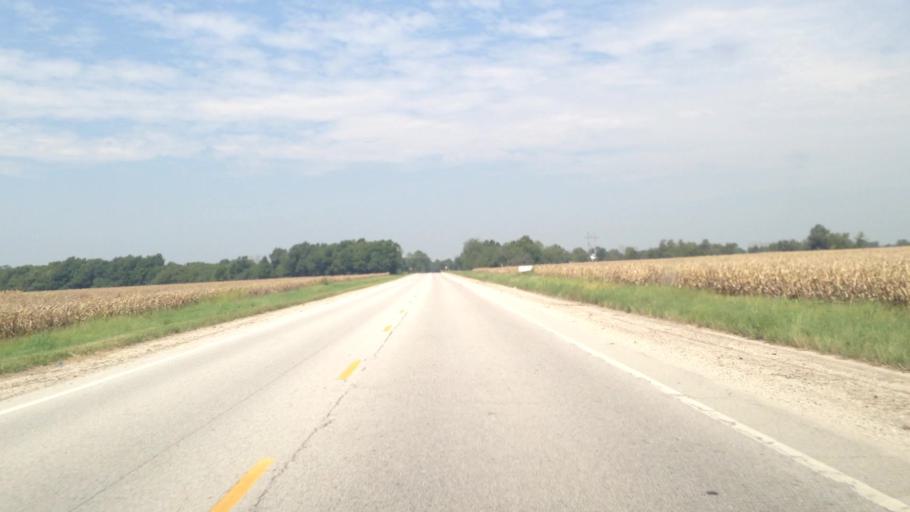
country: US
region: Kansas
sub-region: Labette County
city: Parsons
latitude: 37.3851
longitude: -95.2638
